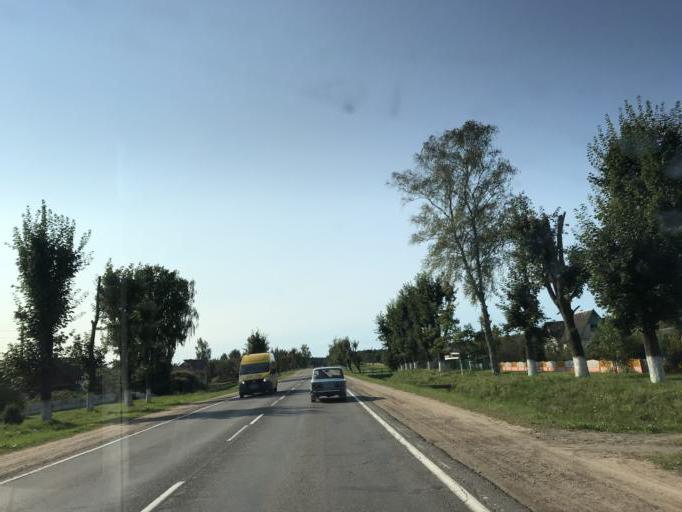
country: BY
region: Mogilev
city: Buynichy
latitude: 53.8283
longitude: 30.2428
